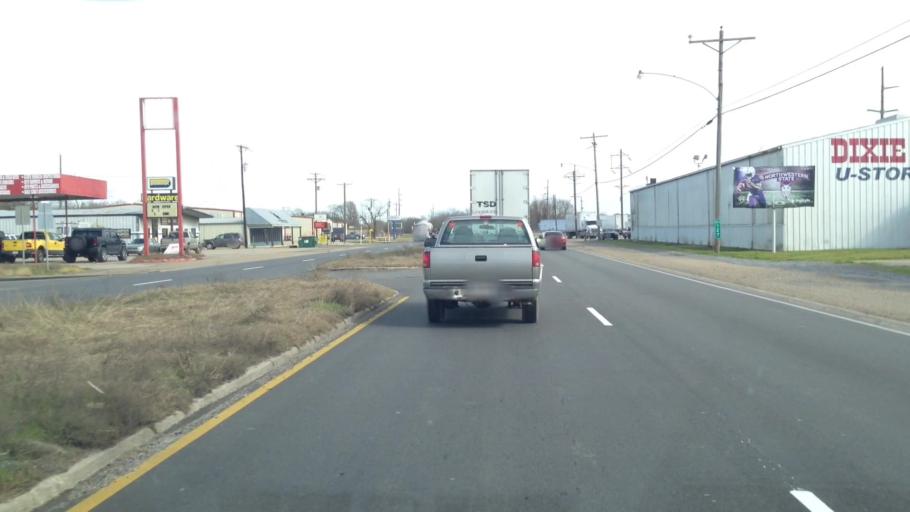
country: US
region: Louisiana
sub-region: Saint Landry Parish
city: Port Barre
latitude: 30.5462
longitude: -91.9619
